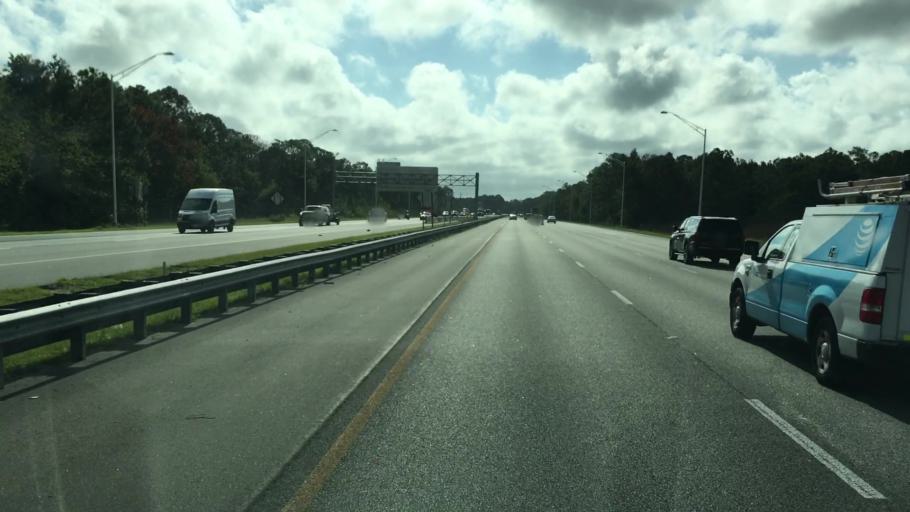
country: US
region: Florida
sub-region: Volusia County
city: South Daytona
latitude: 29.1411
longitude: -81.0676
